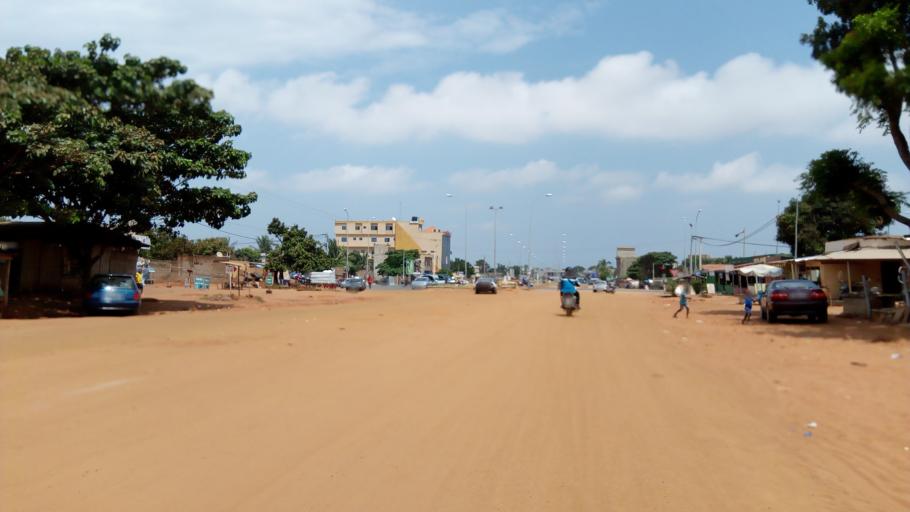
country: TG
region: Maritime
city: Lome
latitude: 6.2156
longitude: 1.1853
